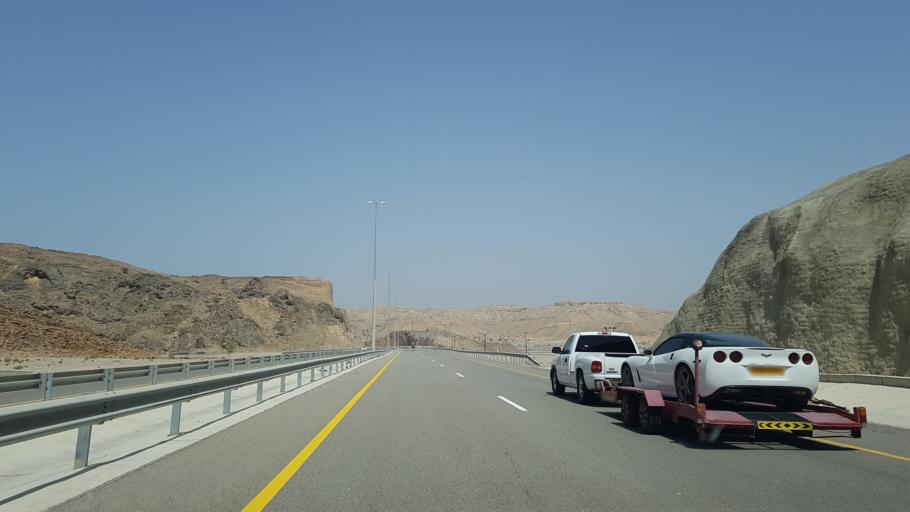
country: OM
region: Muhafazat Masqat
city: Muscat
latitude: 23.1901
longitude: 58.8696
